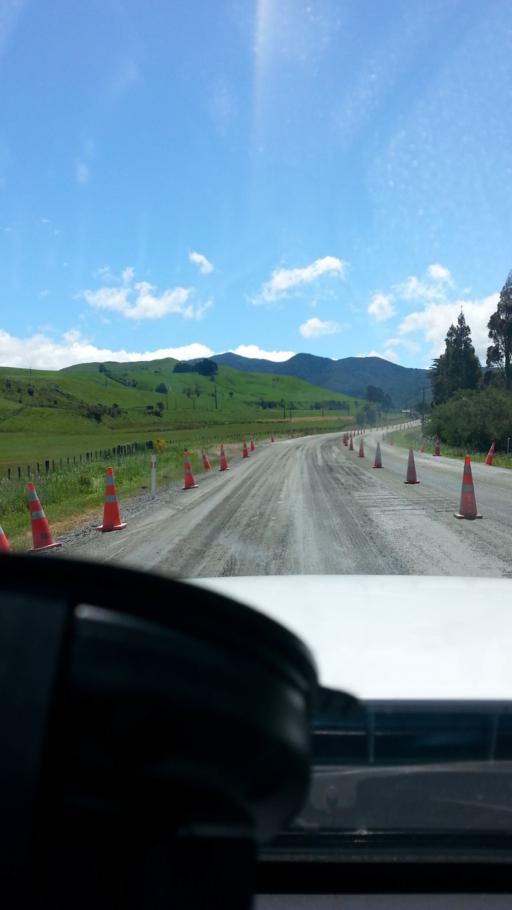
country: NZ
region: Wellington
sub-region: Masterton District
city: Masterton
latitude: -40.7807
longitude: 175.6162
